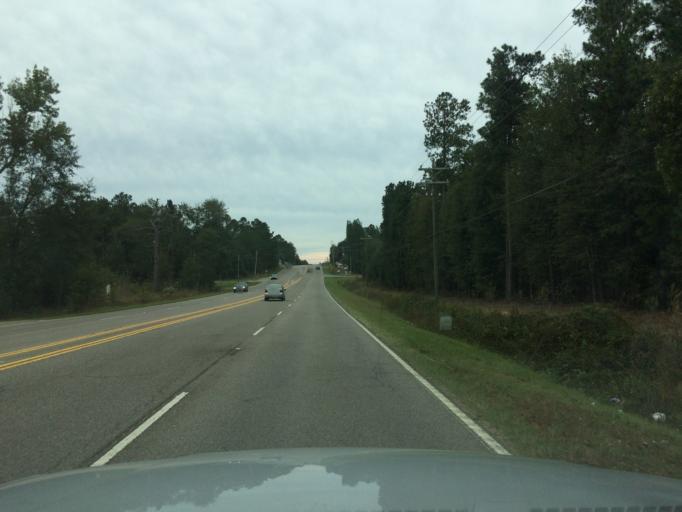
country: US
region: South Carolina
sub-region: Aiken County
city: New Ellenton
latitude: 33.4385
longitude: -81.6863
